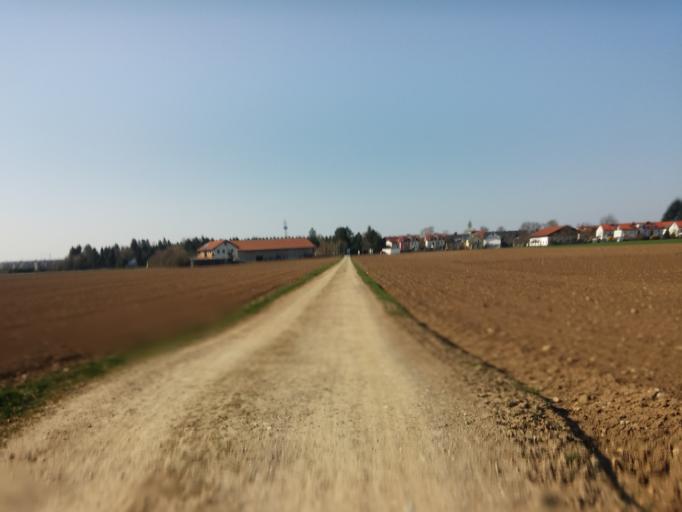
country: DE
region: Bavaria
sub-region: Upper Bavaria
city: Haar
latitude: 48.1260
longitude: 11.7199
